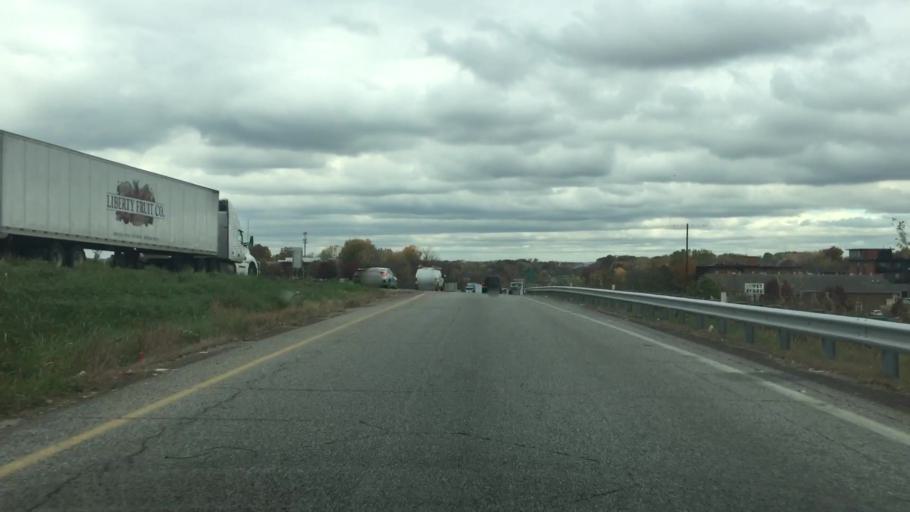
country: US
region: Missouri
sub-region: Jackson County
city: Raytown
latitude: 39.0475
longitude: -94.4455
